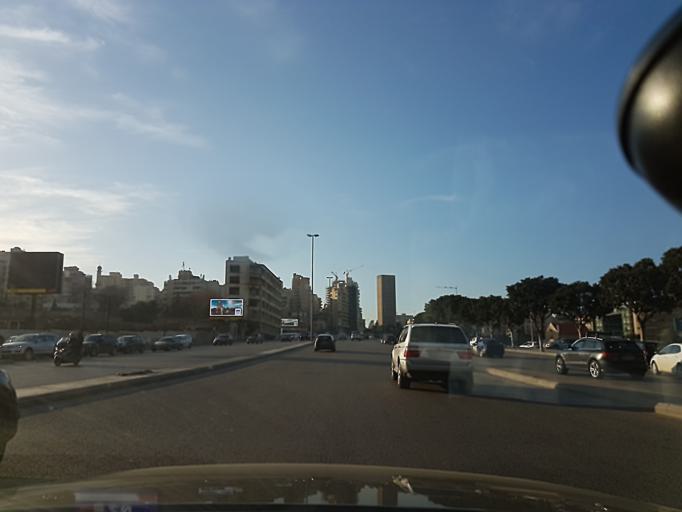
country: LB
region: Beyrouth
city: Beirut
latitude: 33.8926
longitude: 35.5046
